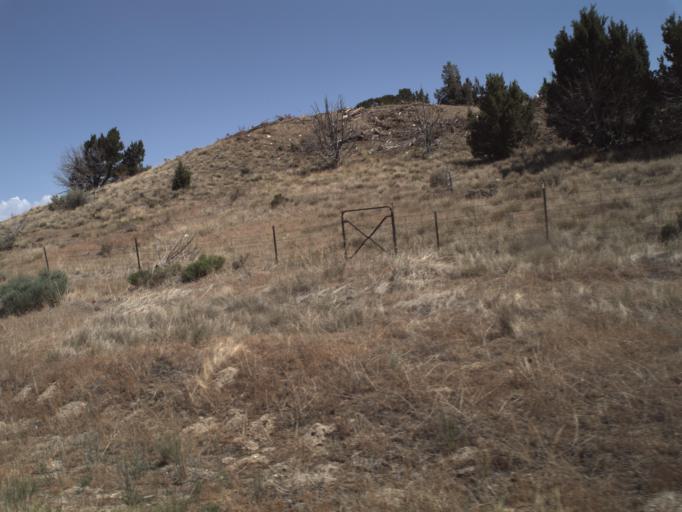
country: US
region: Utah
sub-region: Utah County
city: Genola
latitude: 39.9520
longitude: -112.2378
